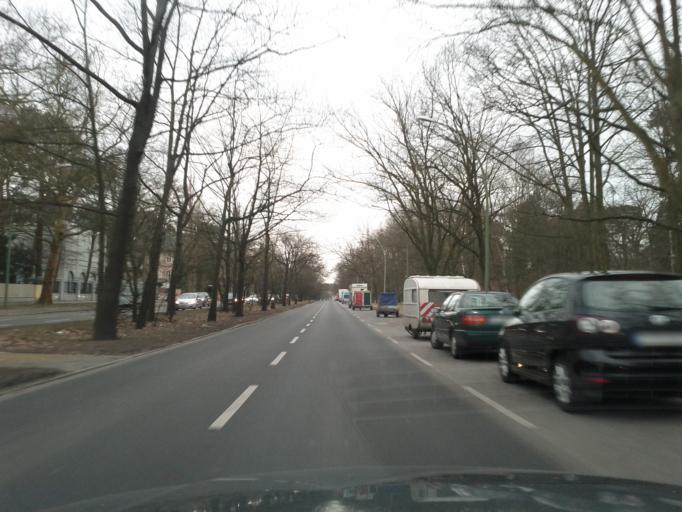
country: DE
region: Berlin
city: Schmargendorf
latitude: 52.4721
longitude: 13.2784
